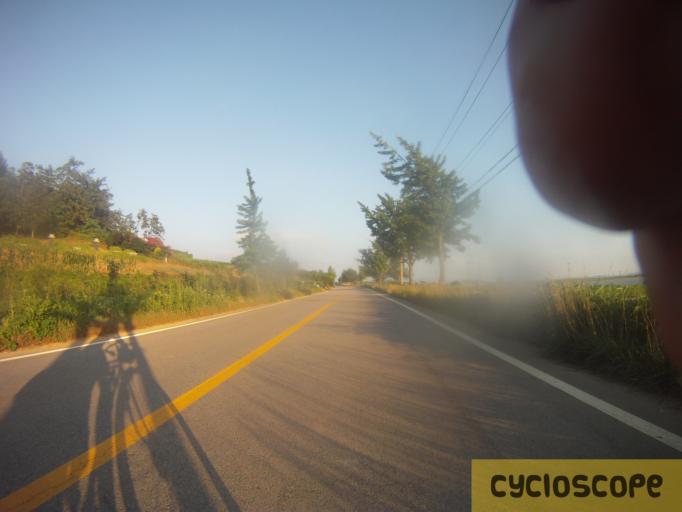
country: KR
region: Jeollanam-do
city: Reiko
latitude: 35.1487
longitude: 126.4114
